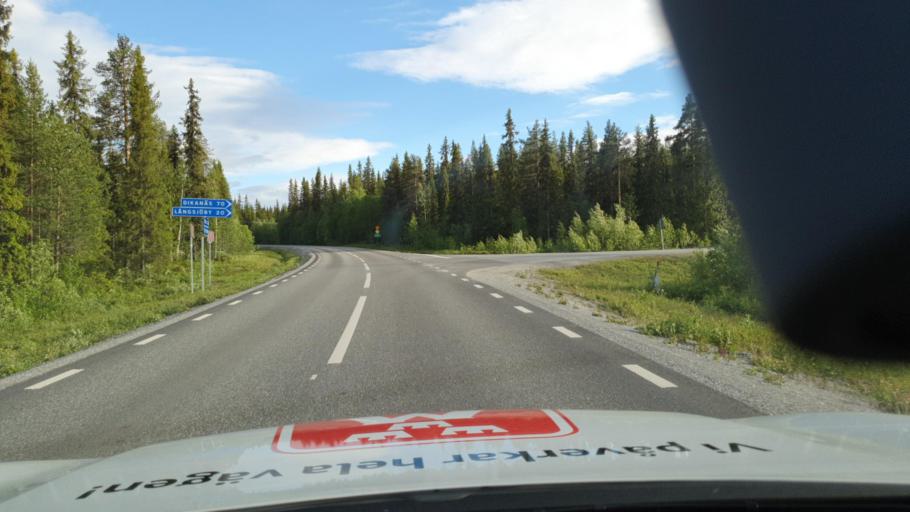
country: SE
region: Vaesterbotten
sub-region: Storumans Kommun
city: Storuman
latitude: 65.0313
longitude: 17.0599
